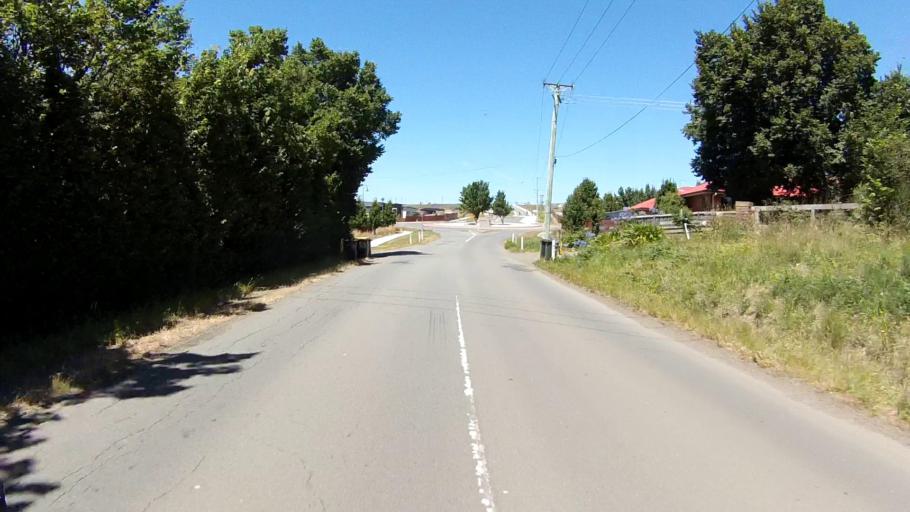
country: AU
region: Tasmania
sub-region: Clarence
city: Howrah
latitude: -42.8830
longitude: 147.4283
